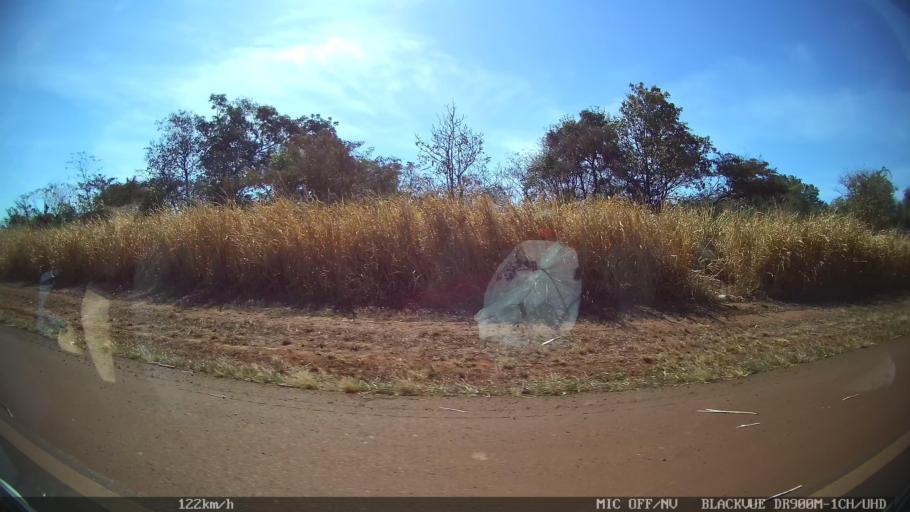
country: BR
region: Sao Paulo
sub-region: Guaira
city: Guaira
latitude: -20.4474
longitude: -48.2042
